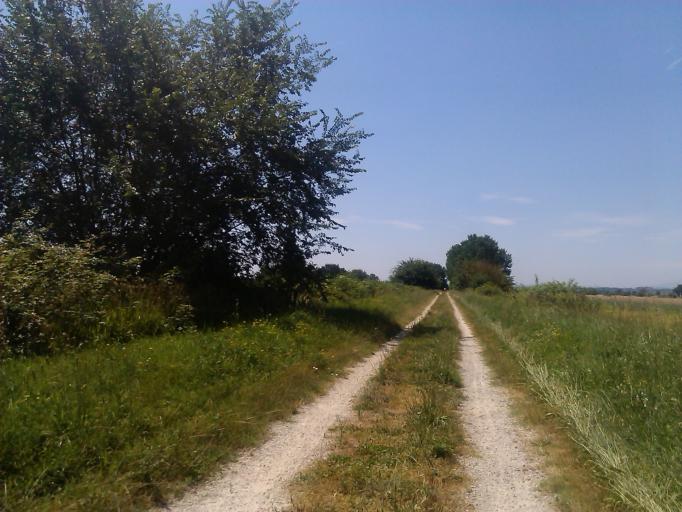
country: IT
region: Tuscany
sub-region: Province of Arezzo
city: Cesa
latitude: 43.3487
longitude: 11.8264
